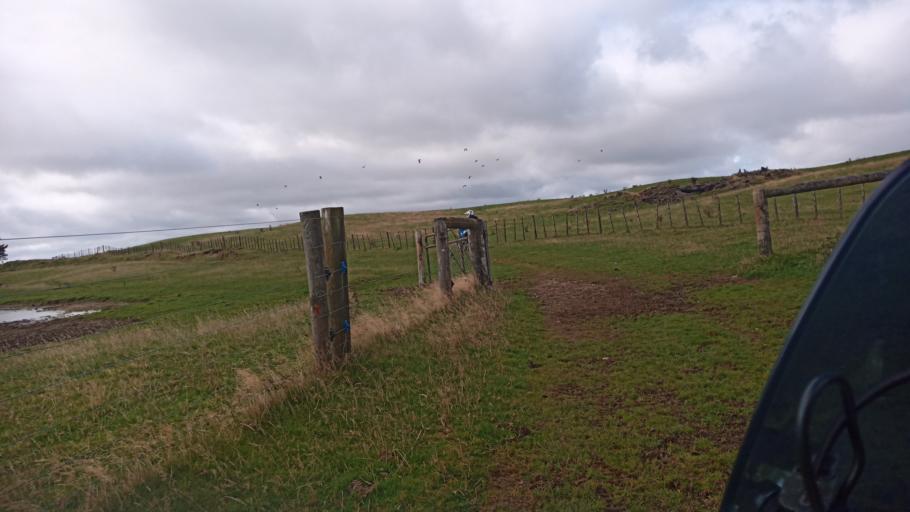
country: NZ
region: Gisborne
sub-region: Gisborne District
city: Gisborne
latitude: -38.4749
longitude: 177.5367
